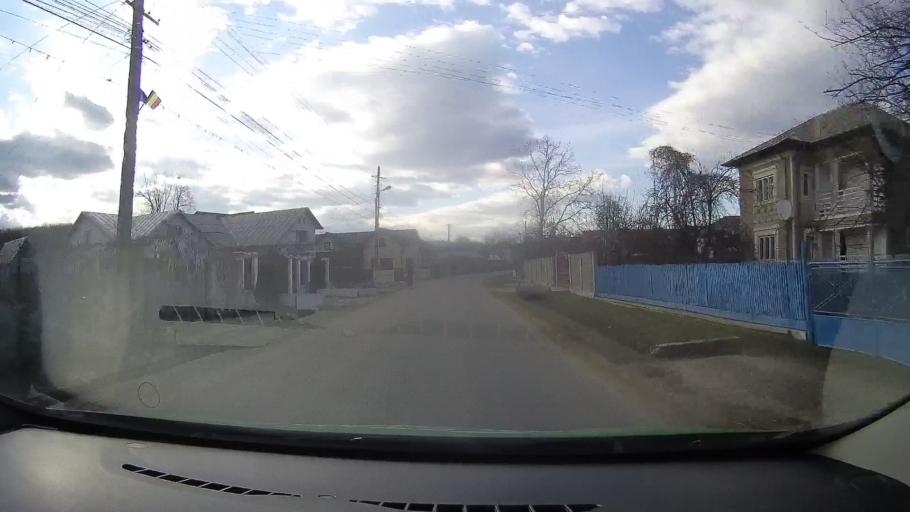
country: RO
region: Dambovita
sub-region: Comuna Ulmi
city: Ulmi
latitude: 44.8837
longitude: 25.5125
